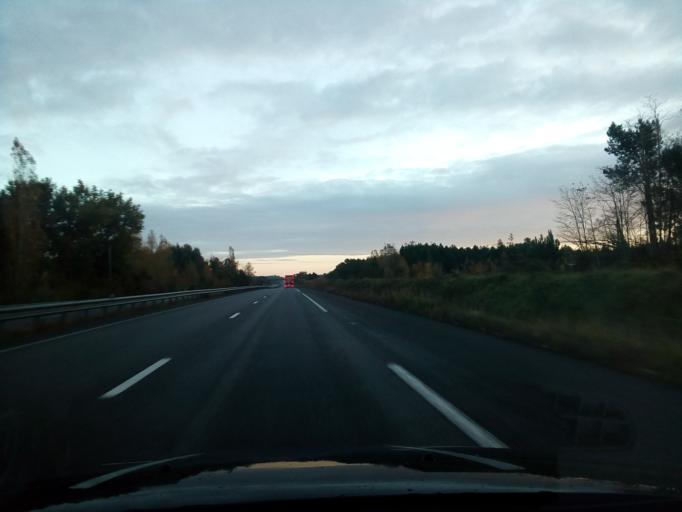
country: FR
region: Poitou-Charentes
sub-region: Departement de la Charente-Maritime
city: Montlieu-la-Garde
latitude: 45.1997
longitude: -0.3044
